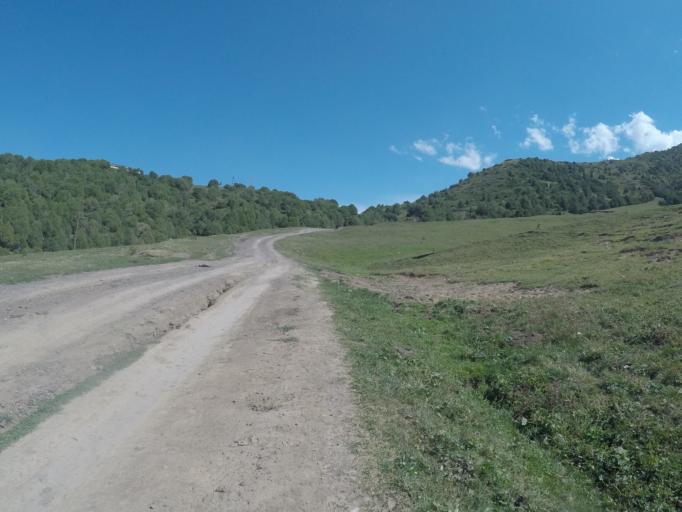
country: KG
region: Chuy
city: Bishkek
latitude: 42.6479
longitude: 74.5574
